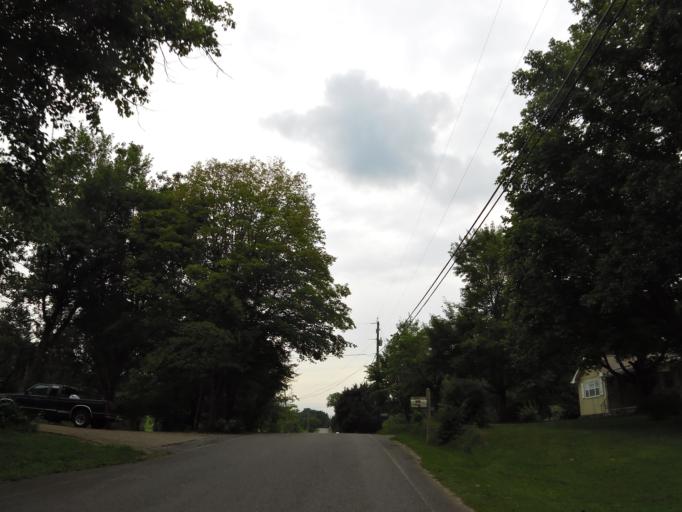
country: US
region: Tennessee
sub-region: Sevier County
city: Seymour
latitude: 35.9190
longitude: -83.8092
